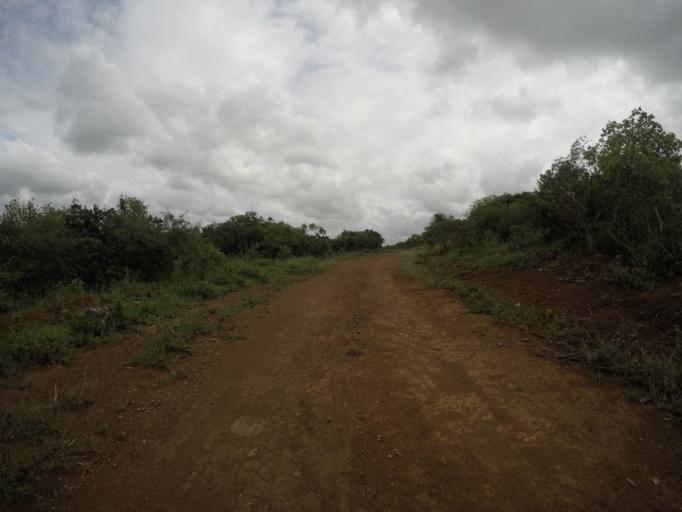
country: ZA
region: KwaZulu-Natal
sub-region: uThungulu District Municipality
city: Empangeni
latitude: -28.5859
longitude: 31.8690
